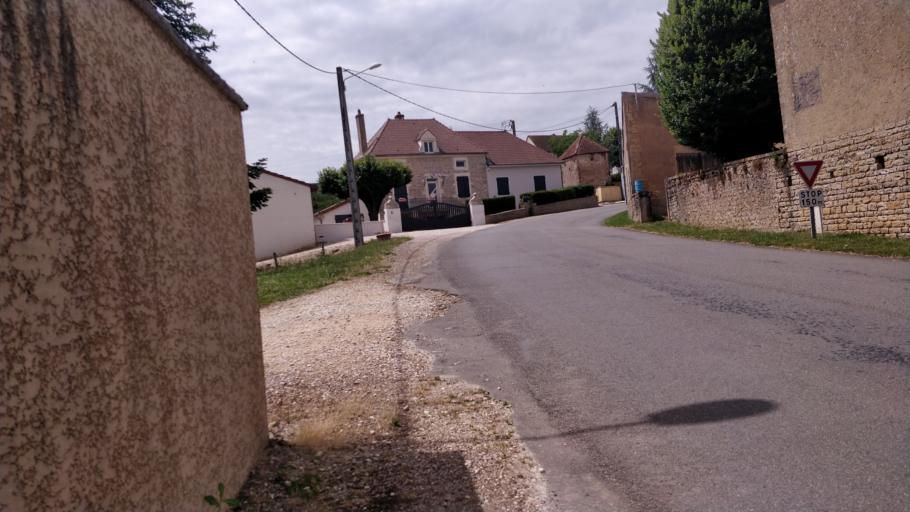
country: FR
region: Bourgogne
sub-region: Departement de Saone-et-Loire
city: Buxy
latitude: 46.7316
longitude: 4.6856
